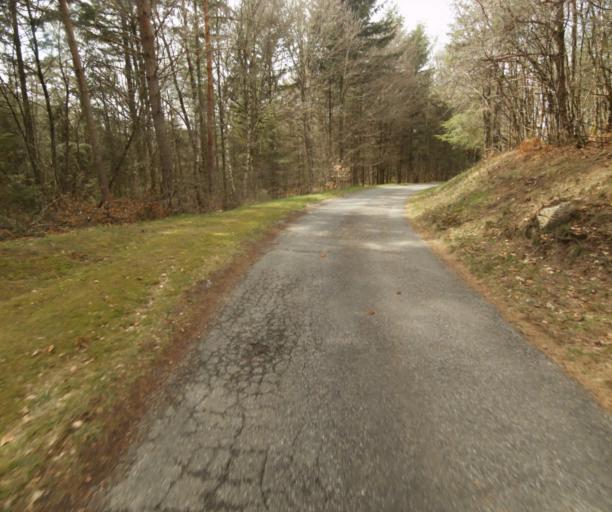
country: FR
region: Limousin
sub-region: Departement de la Correze
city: Argentat
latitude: 45.2192
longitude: 1.9121
